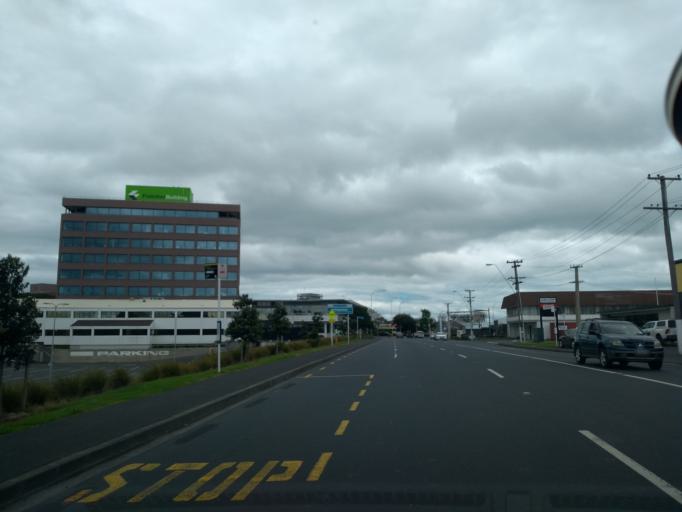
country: NZ
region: Auckland
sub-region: Auckland
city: Tamaki
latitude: -36.9101
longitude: 174.8194
